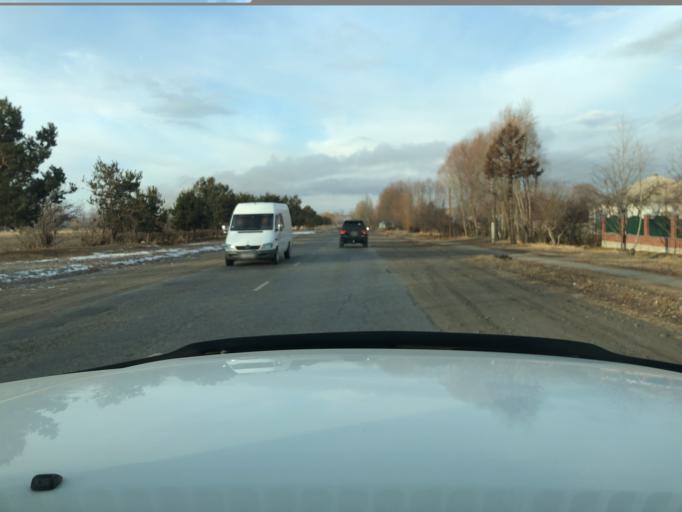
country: KG
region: Ysyk-Koel
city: Karakol
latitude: 42.4821
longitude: 78.3582
